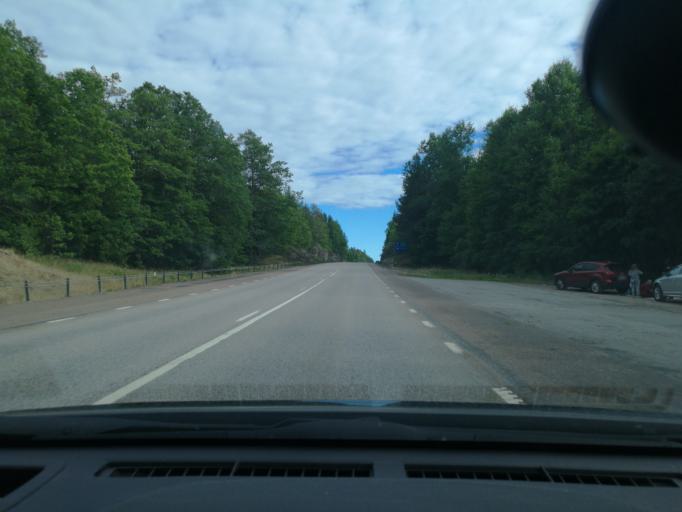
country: SE
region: Kalmar
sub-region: Vasterviks Kommun
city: Ankarsrum
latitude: 57.5493
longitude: 16.4770
